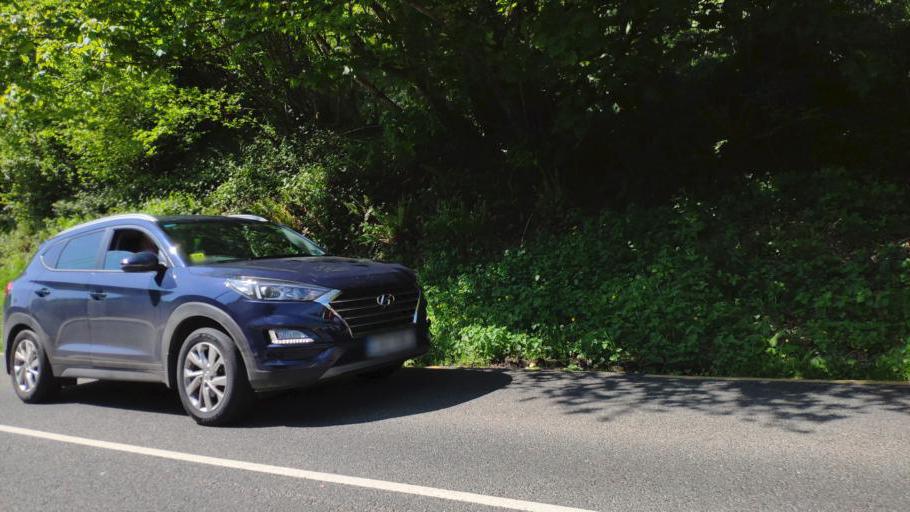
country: IE
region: Munster
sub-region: County Cork
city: Blarney
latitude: 51.9532
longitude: -8.5737
